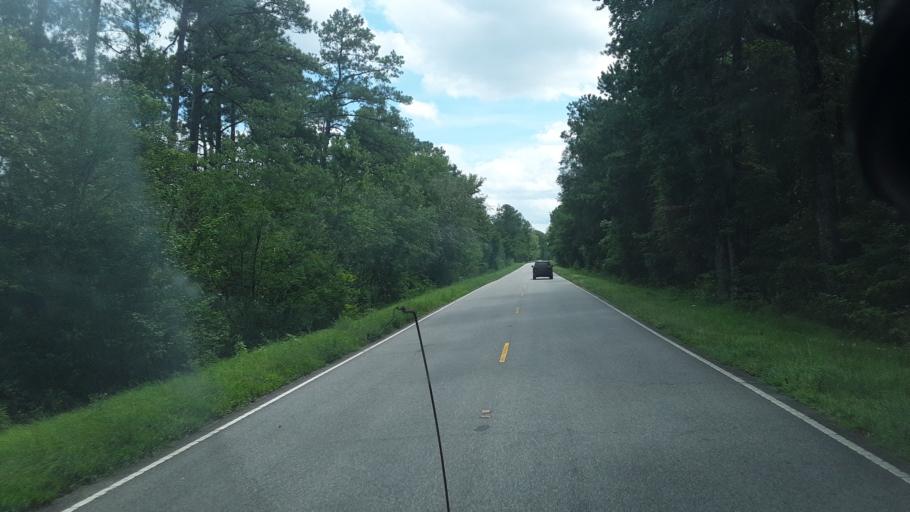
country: US
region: North Carolina
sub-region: Robeson County
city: Fairmont
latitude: 34.3355
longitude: -79.0564
